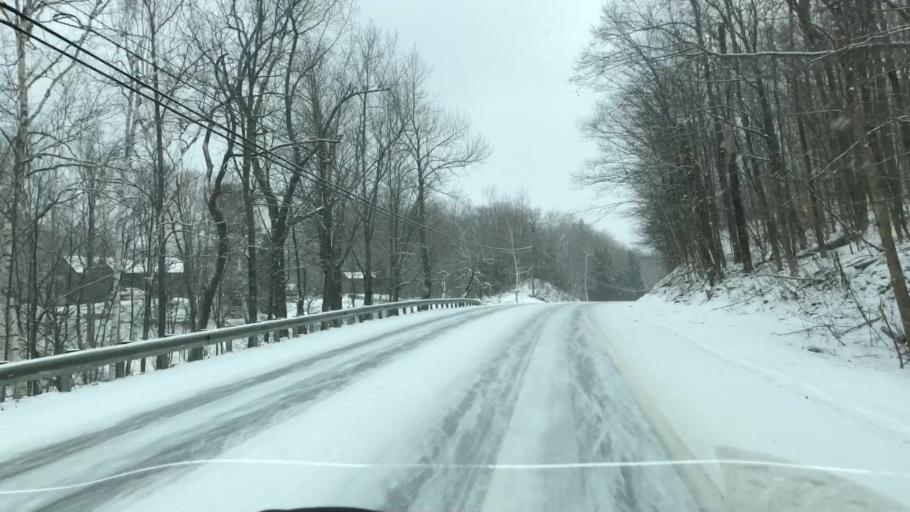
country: US
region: Massachusetts
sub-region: Berkshire County
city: Adams
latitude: 42.5813
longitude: -73.0638
